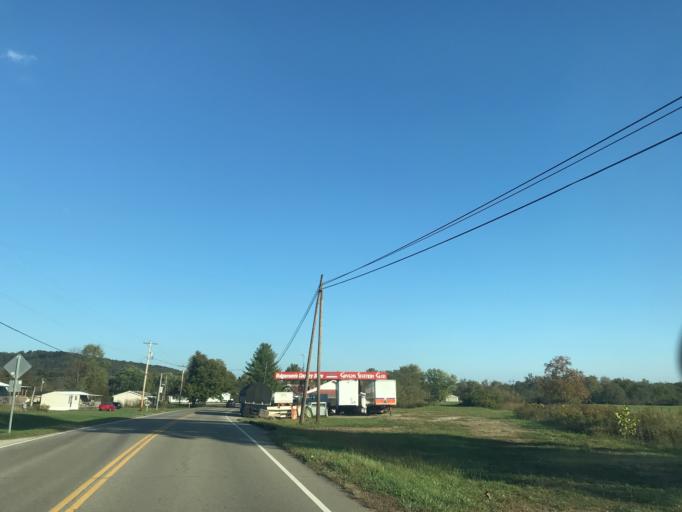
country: US
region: Ohio
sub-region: Pike County
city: Piketon
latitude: 39.0529
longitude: -82.9227
